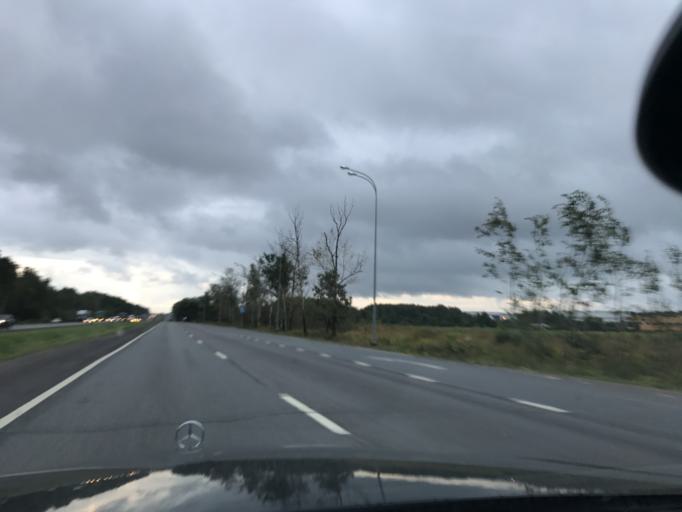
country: RU
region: Moskovskaya
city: Noginsk
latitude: 55.8439
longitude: 38.4846
